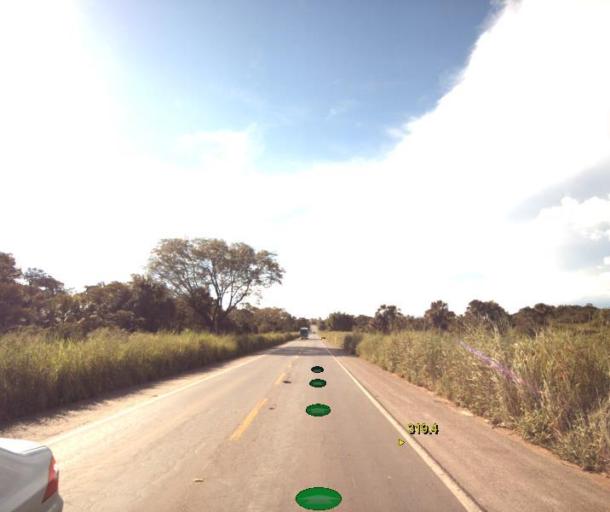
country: BR
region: Goias
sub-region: Rialma
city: Rialma
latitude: -15.4350
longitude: -49.5106
